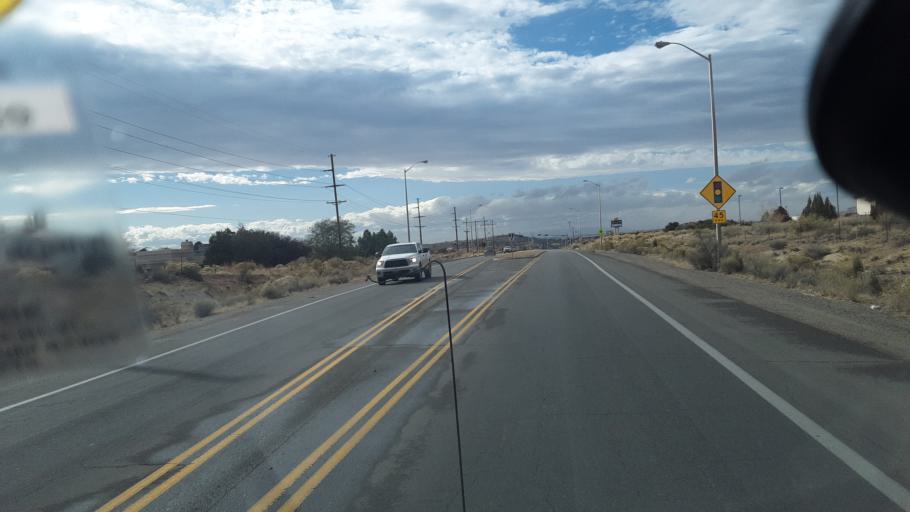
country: US
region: New Mexico
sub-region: San Juan County
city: Farmington
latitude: 36.7737
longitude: -108.1902
